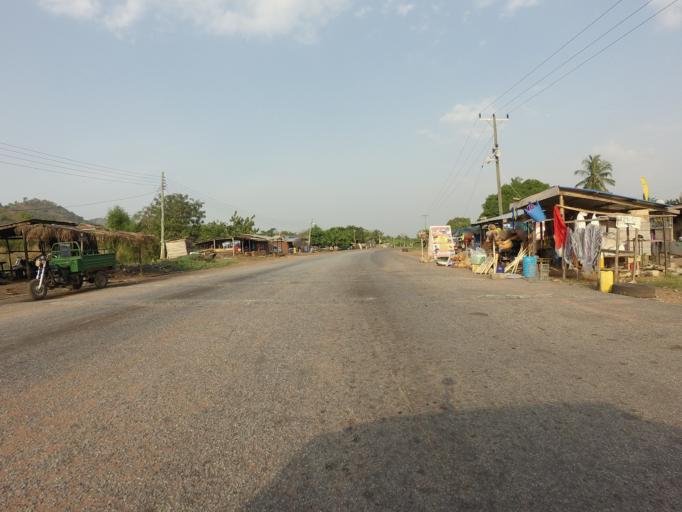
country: GH
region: Volta
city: Ho
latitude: 6.4165
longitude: 0.1741
